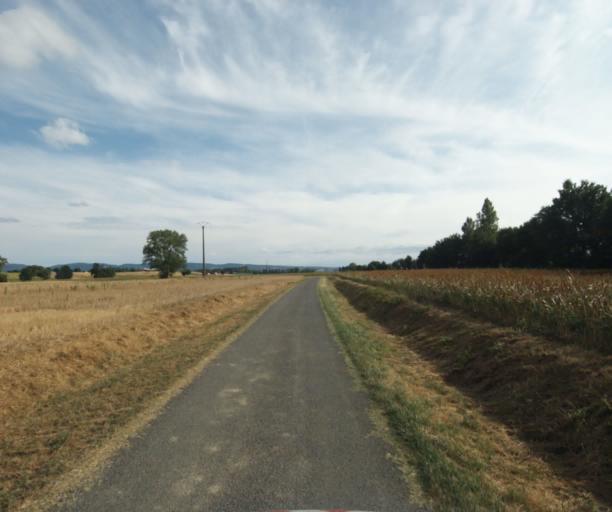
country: FR
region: Midi-Pyrenees
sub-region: Departement du Tarn
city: Puylaurens
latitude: 43.5169
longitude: 1.9906
